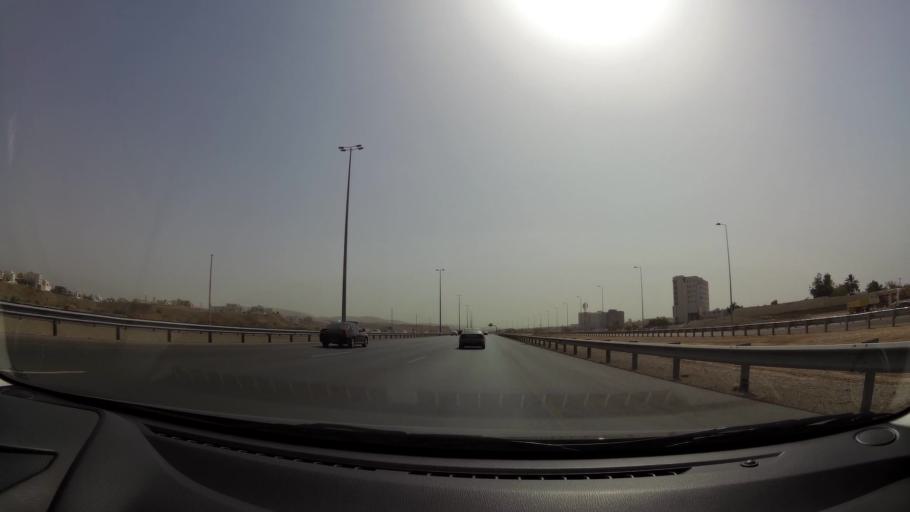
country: OM
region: Muhafazat Masqat
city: Bawshar
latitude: 23.5650
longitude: 58.3560
